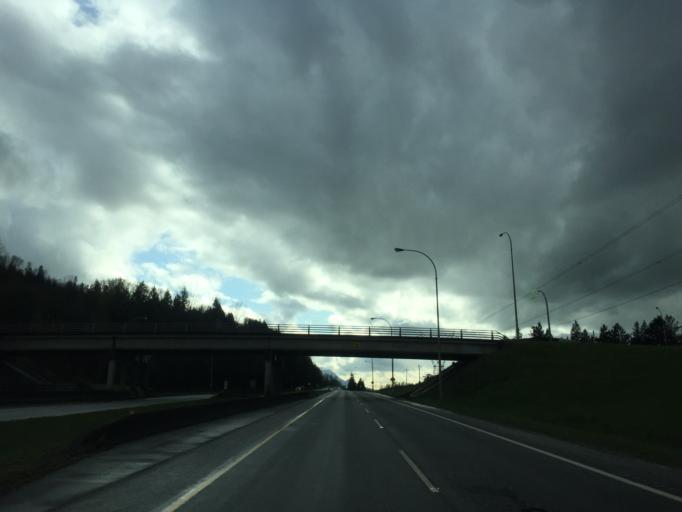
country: CA
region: British Columbia
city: Agassiz
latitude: 49.1814
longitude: -121.7606
